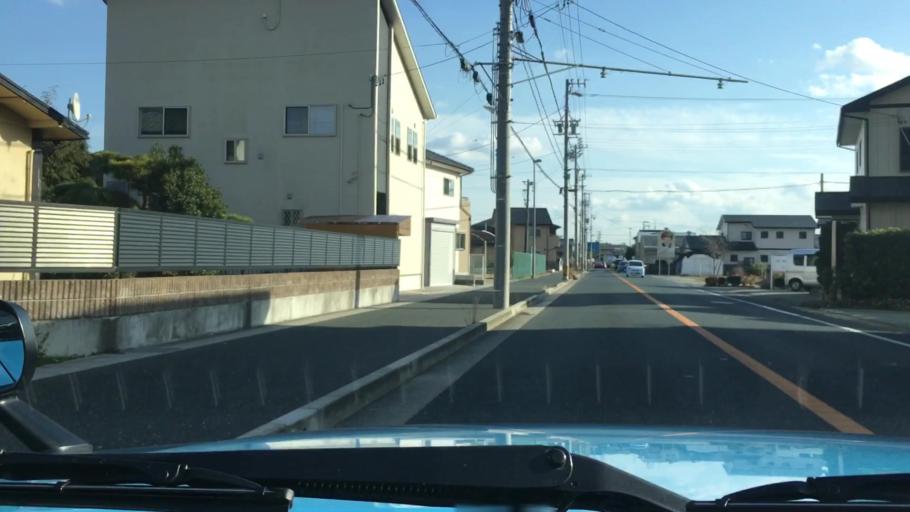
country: JP
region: Shizuoka
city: Hamamatsu
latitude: 34.7543
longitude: 137.6708
